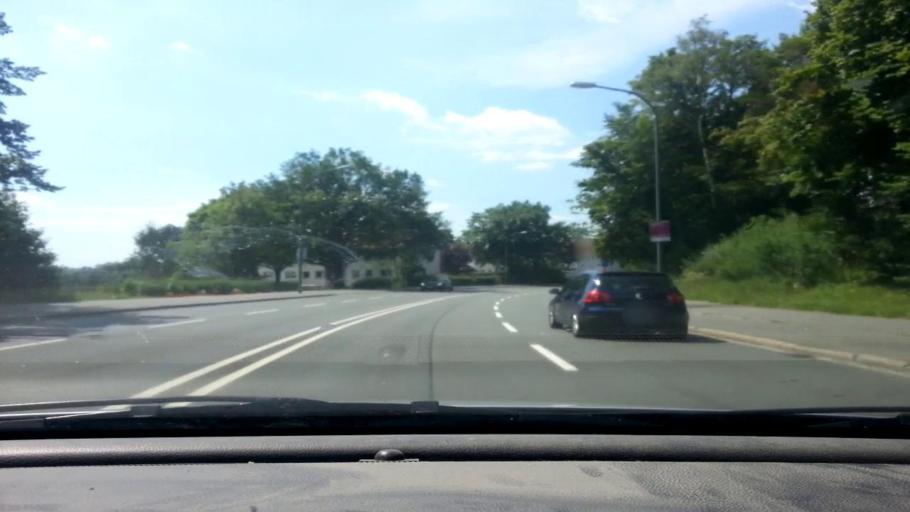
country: DE
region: Bavaria
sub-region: Upper Franconia
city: Bayreuth
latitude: 49.9503
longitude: 11.5986
